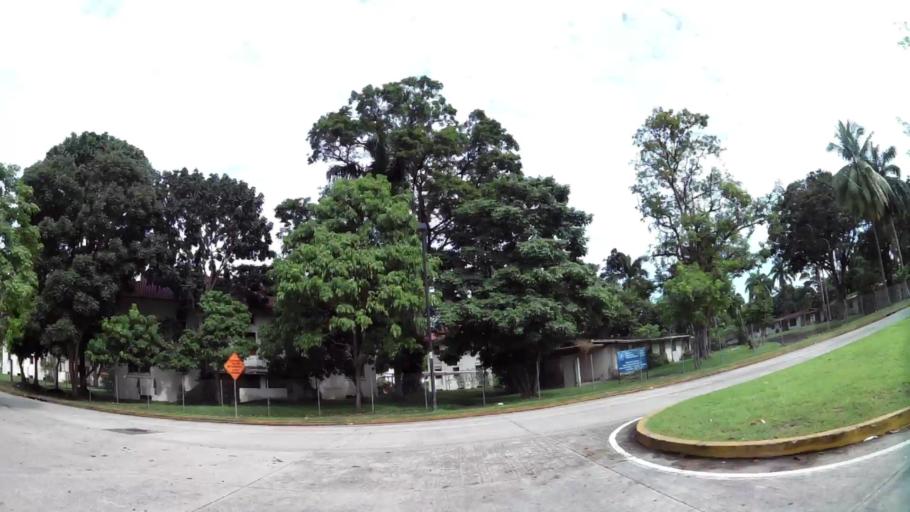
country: PA
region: Panama
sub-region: Distrito de Panama
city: Ancon
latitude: 8.9406
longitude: -79.5500
